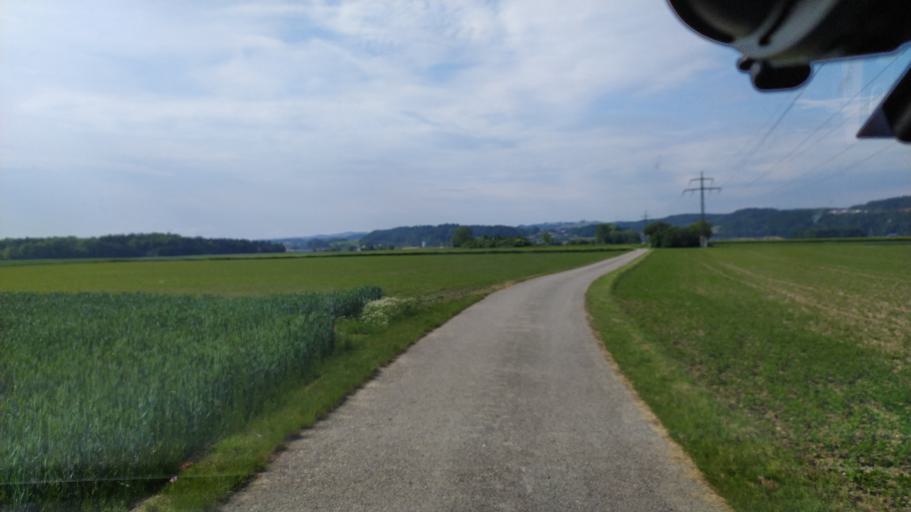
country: AT
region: Lower Austria
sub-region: Politischer Bezirk Amstetten
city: Zeillern
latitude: 48.1918
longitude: 14.7595
